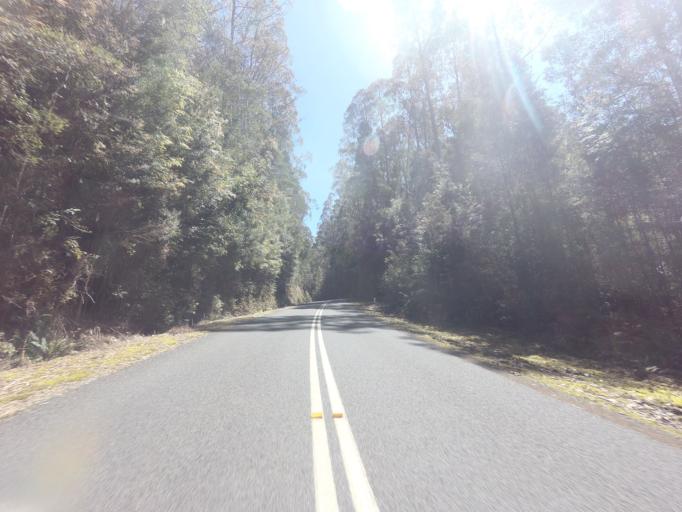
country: AU
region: Tasmania
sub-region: Huon Valley
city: Geeveston
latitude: -42.8199
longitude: 146.2879
